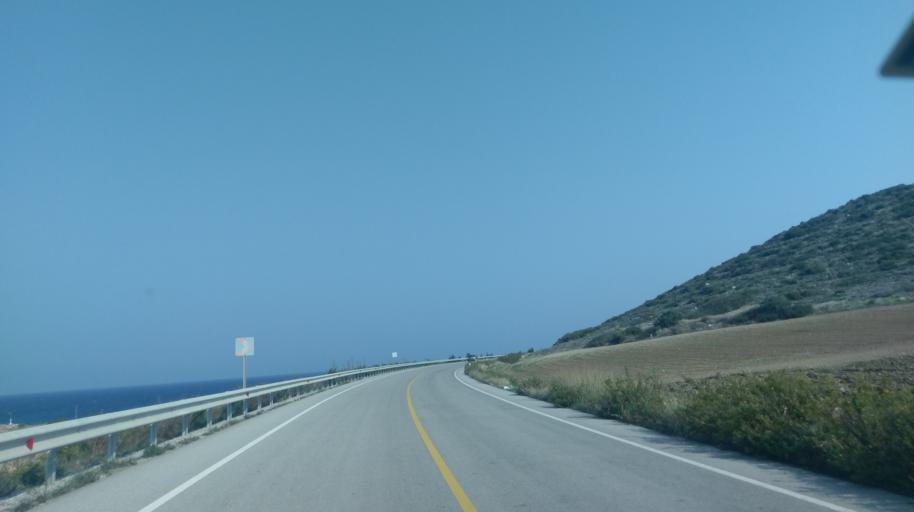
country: CY
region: Ammochostos
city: Leonarisso
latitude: 35.4902
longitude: 34.0807
